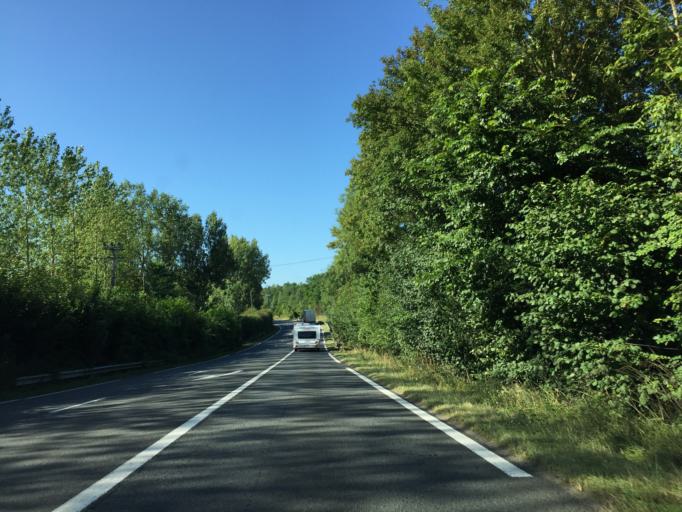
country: FR
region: Lower Normandy
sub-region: Departement du Calvados
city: Saint-Gatien-des-Bois
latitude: 49.2784
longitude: 0.2153
